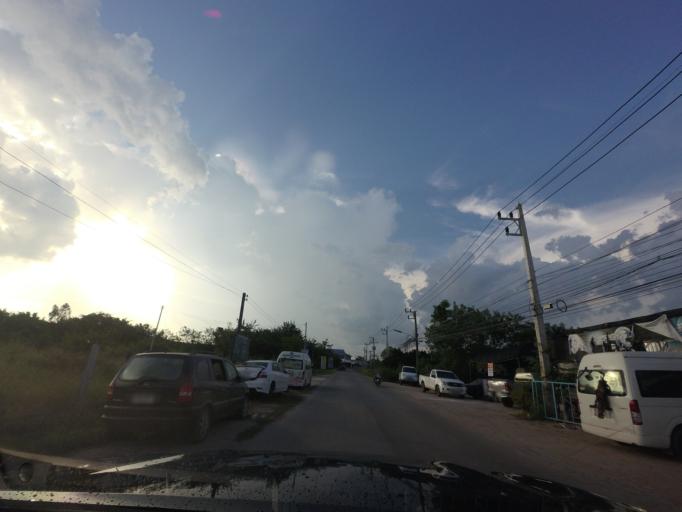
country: TH
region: Khon Kaen
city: Khon Kaen
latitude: 16.4019
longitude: 102.8663
